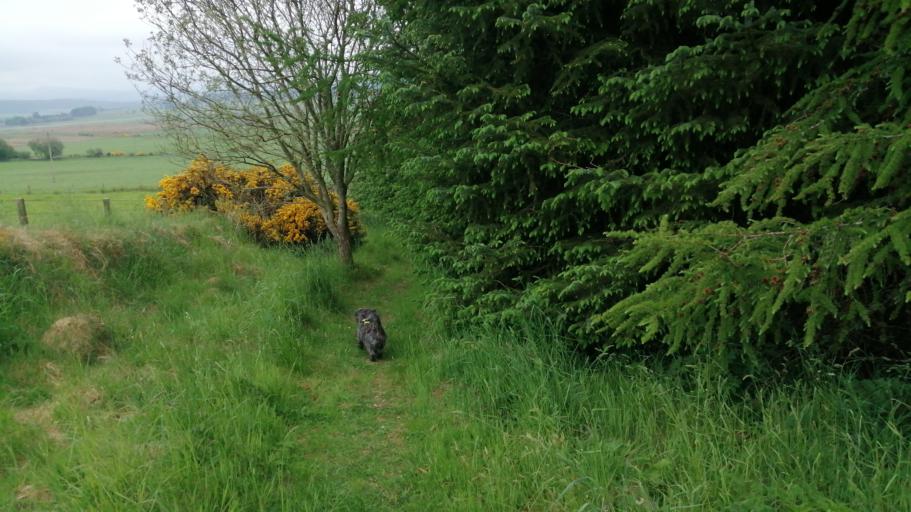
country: GB
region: Scotland
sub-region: Moray
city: Cullen
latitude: 57.5780
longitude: -2.7870
